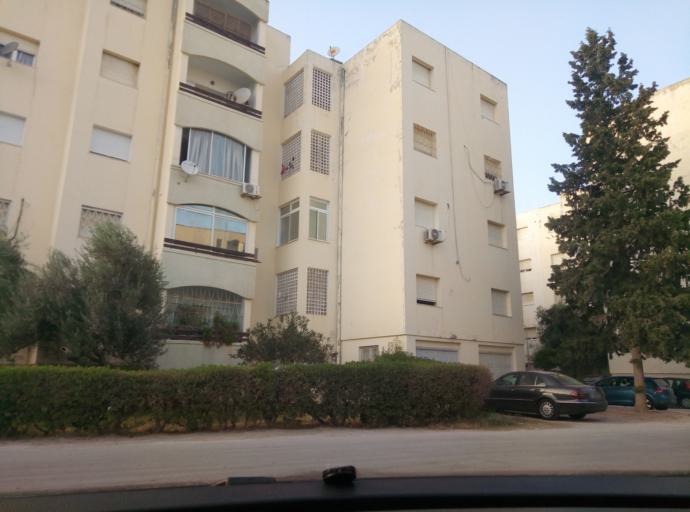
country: TN
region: Tunis
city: La Goulette
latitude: 36.8557
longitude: 10.2680
